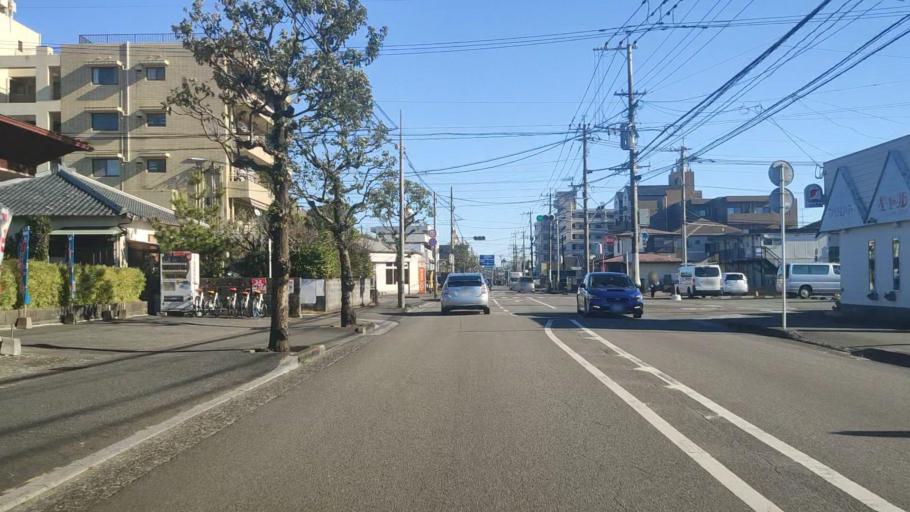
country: JP
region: Miyazaki
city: Miyazaki-shi
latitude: 31.8966
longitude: 131.4292
